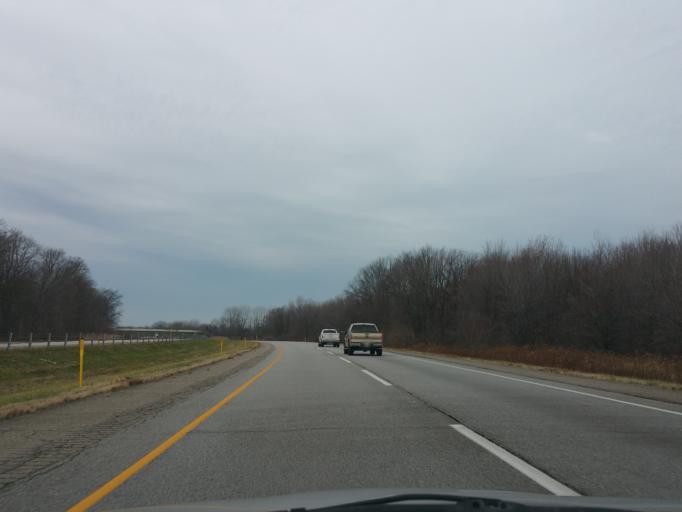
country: US
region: Indiana
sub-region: Porter County
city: Chesterton
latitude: 41.5789
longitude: -87.0696
